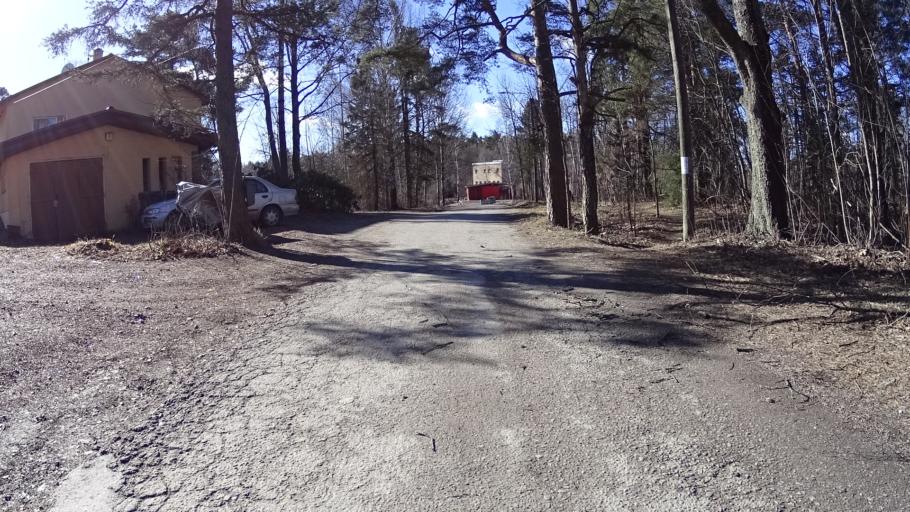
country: FI
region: Uusimaa
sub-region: Helsinki
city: Teekkarikylae
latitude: 60.2574
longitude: 24.8738
